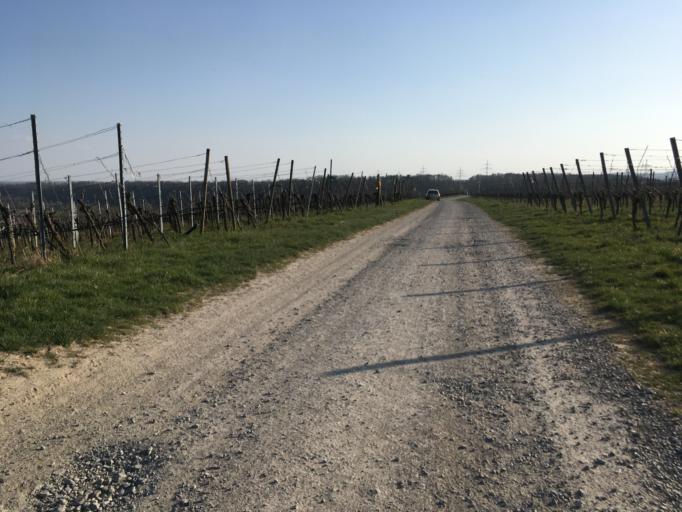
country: DE
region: Baden-Wuerttemberg
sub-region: Regierungsbezirk Stuttgart
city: Lauffen am Neckar
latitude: 49.0750
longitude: 9.1293
